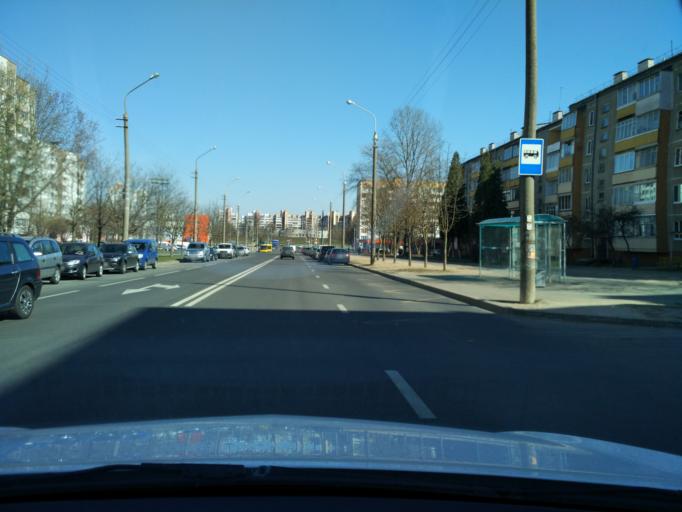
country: BY
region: Minsk
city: Minsk
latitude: 53.8774
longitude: 27.5567
